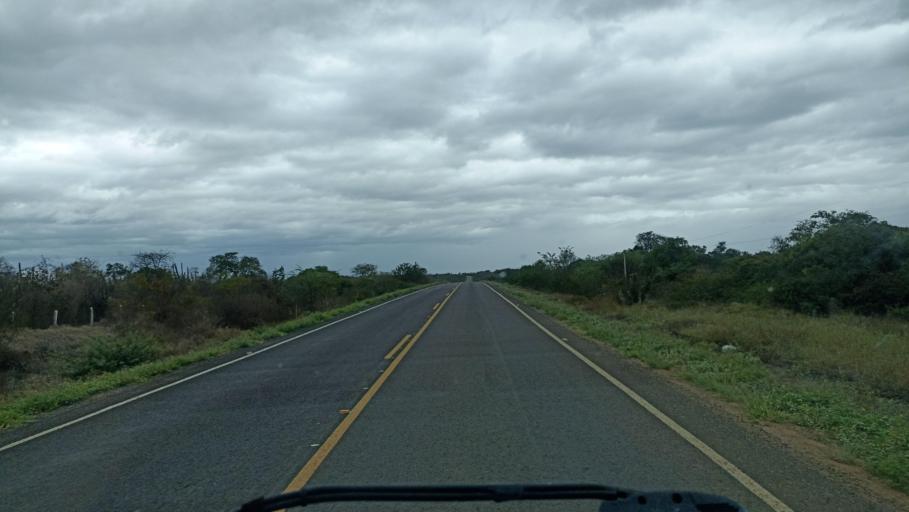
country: BR
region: Bahia
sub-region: Iacu
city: Iacu
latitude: -12.9719
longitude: -40.5030
